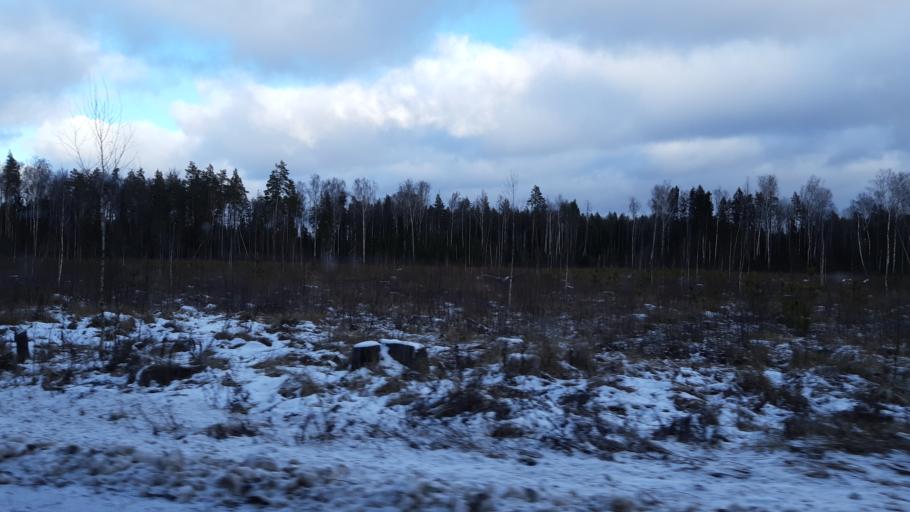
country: RU
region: Moskovskaya
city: Noginsk-9
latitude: 55.9682
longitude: 38.5374
